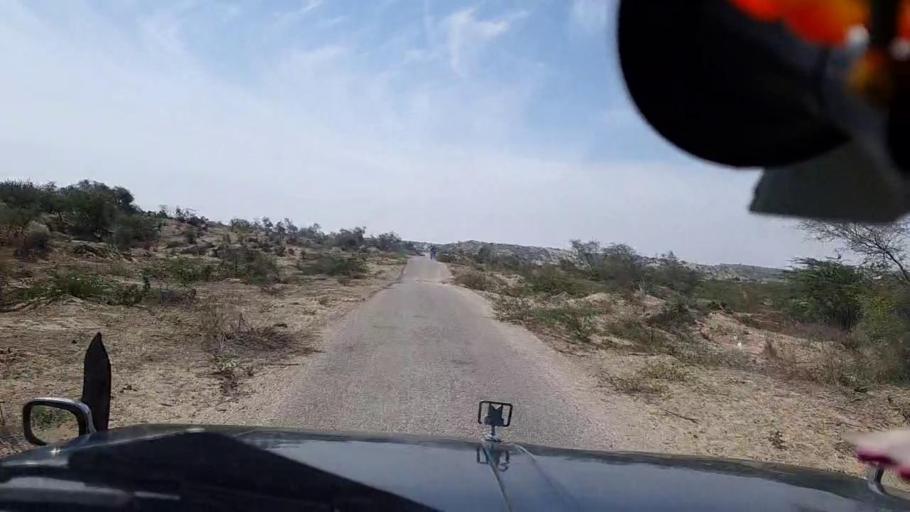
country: PK
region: Sindh
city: Diplo
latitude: 24.3760
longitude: 69.5841
